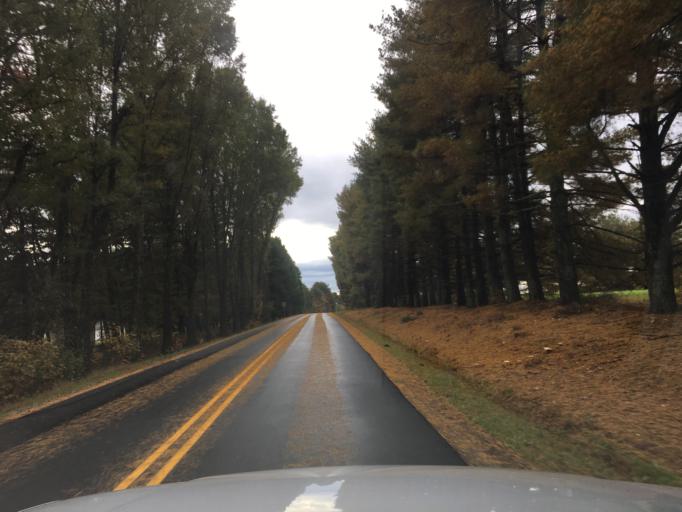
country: US
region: North Carolina
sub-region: Catawba County
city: Maiden
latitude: 35.6179
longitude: -81.2265
